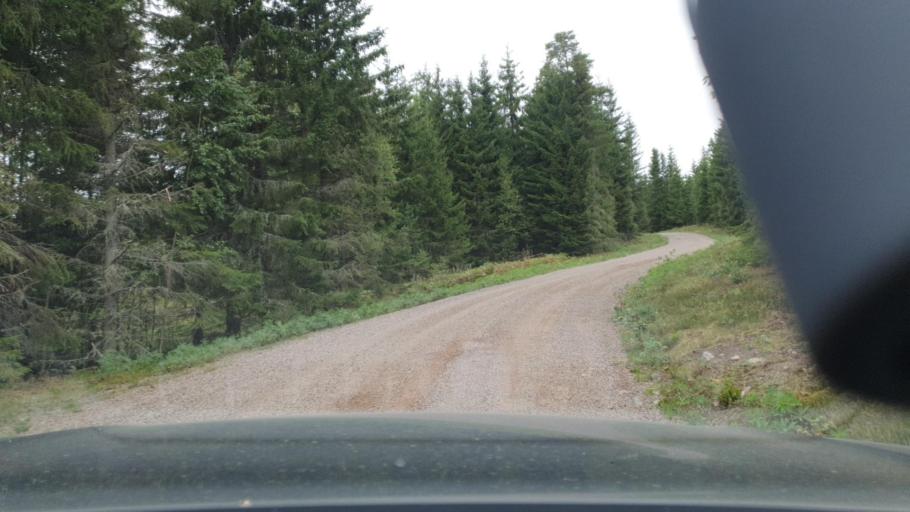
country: SE
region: Vaermland
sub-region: Torsby Kommun
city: Torsby
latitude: 59.9515
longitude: 12.7808
